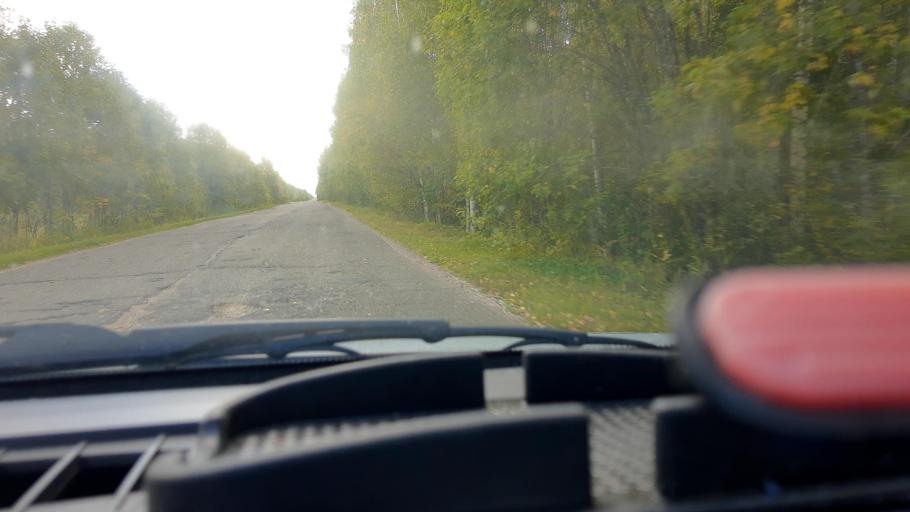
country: RU
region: Mariy-El
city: Kilemary
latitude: 56.9087
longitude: 46.7320
